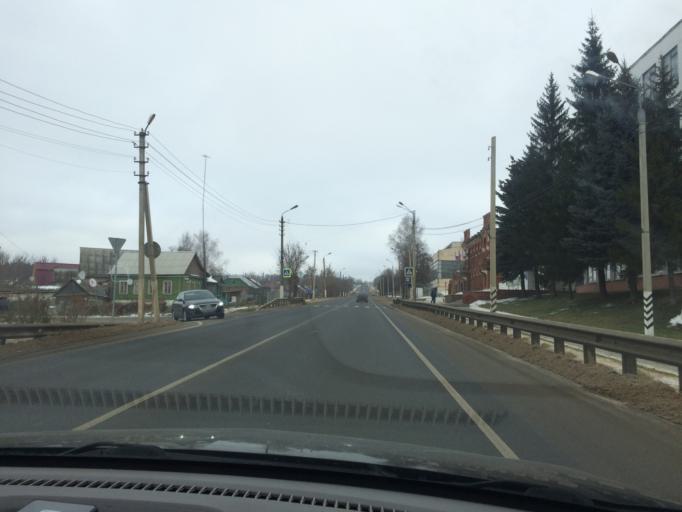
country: RU
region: Tula
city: Plavsk
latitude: 53.7126
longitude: 37.2962
